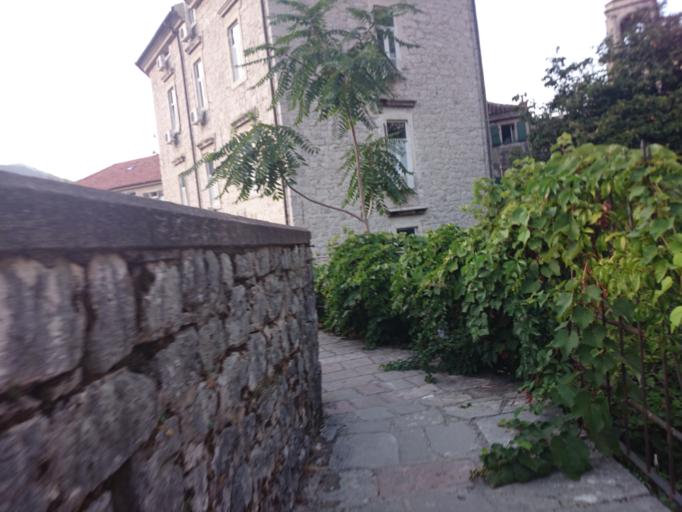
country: ME
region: Kotor
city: Kotor
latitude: 42.4235
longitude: 18.7712
